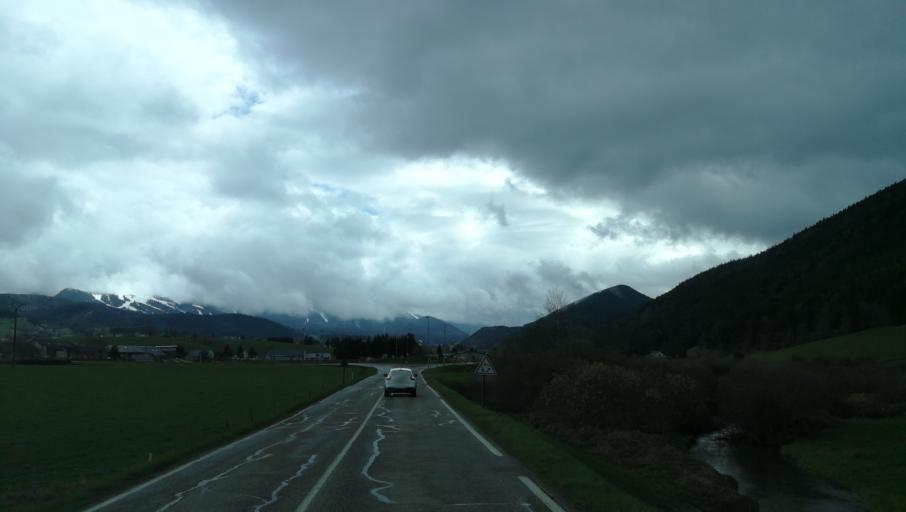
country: FR
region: Rhone-Alpes
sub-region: Departement de l'Isere
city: Villard-de-Lans
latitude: 45.0919
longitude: 5.5560
